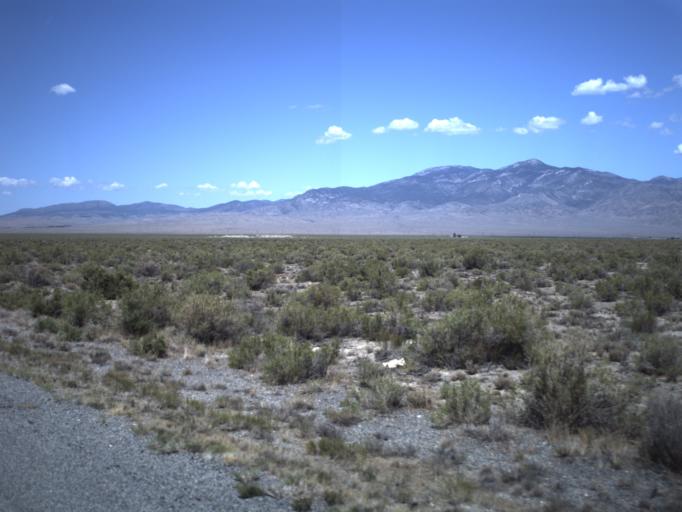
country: US
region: Nevada
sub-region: White Pine County
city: McGill
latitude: 39.0548
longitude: -114.0186
